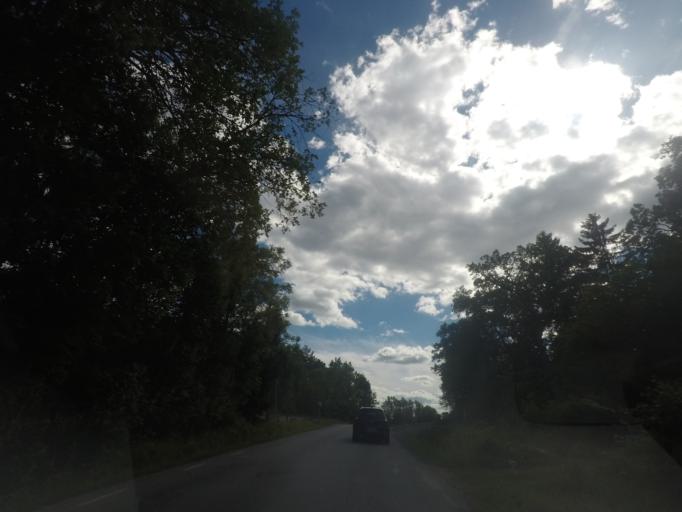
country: SE
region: Stockholm
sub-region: Norrtalje Kommun
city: Arno
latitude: 60.1051
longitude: 18.8088
